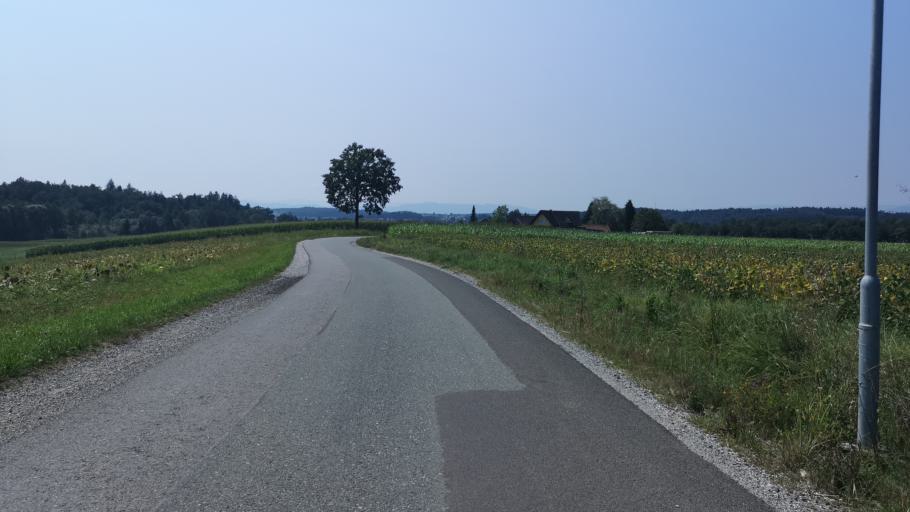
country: AT
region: Styria
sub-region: Politischer Bezirk Deutschlandsberg
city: Preding
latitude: 46.8614
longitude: 15.3895
